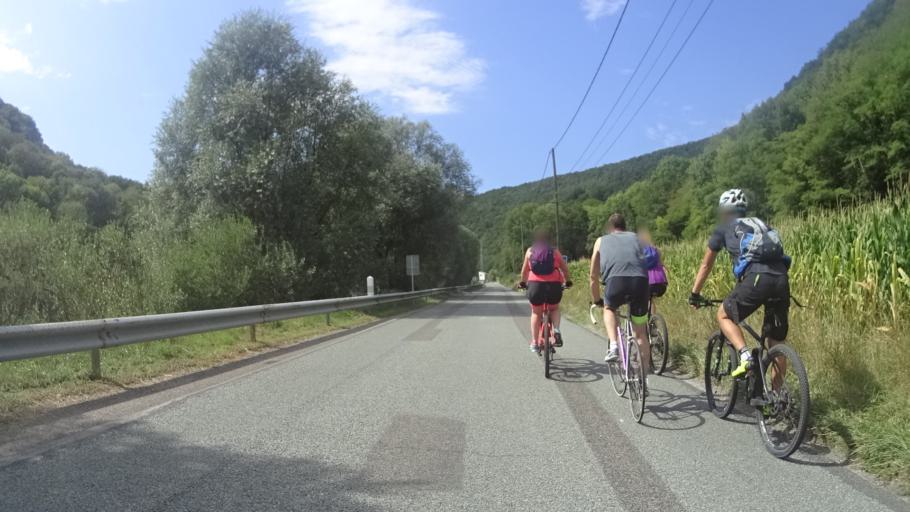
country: FR
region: Franche-Comte
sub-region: Departement du Doubs
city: Roulans
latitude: 47.3002
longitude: 6.2194
